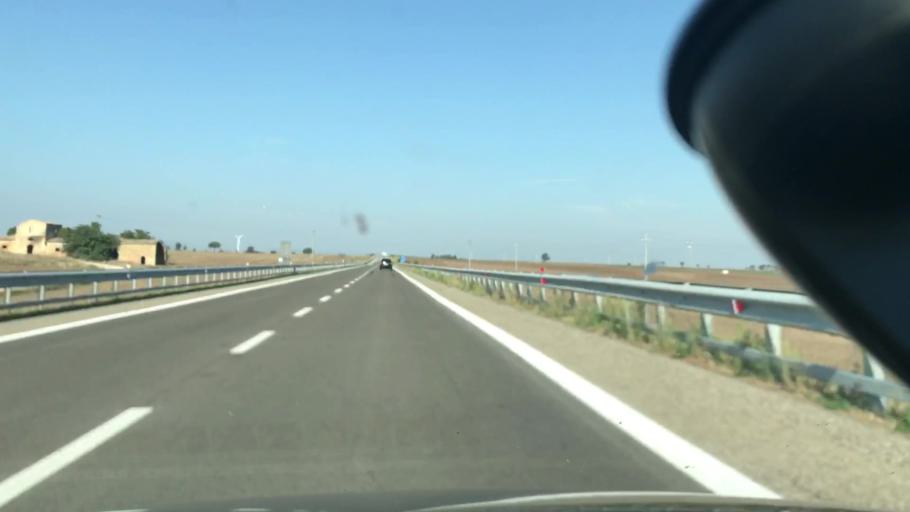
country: IT
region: Basilicate
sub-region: Provincia di Potenza
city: Montemilone
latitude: 40.9877
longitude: 15.9090
